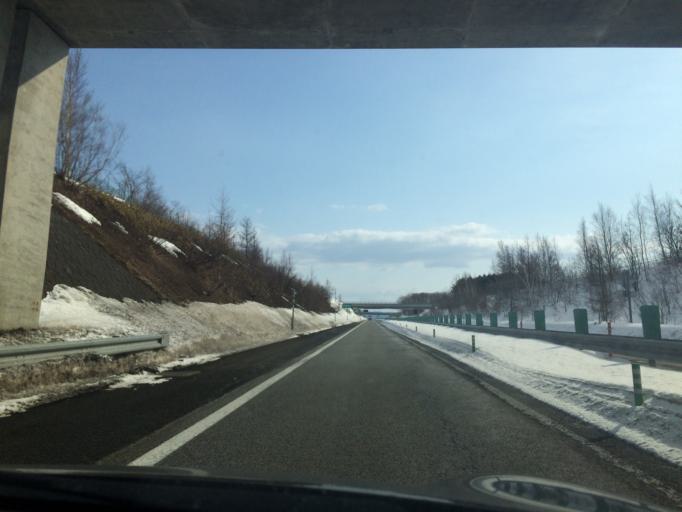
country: JP
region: Hokkaido
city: Chitose
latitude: 42.8931
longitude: 141.8021
